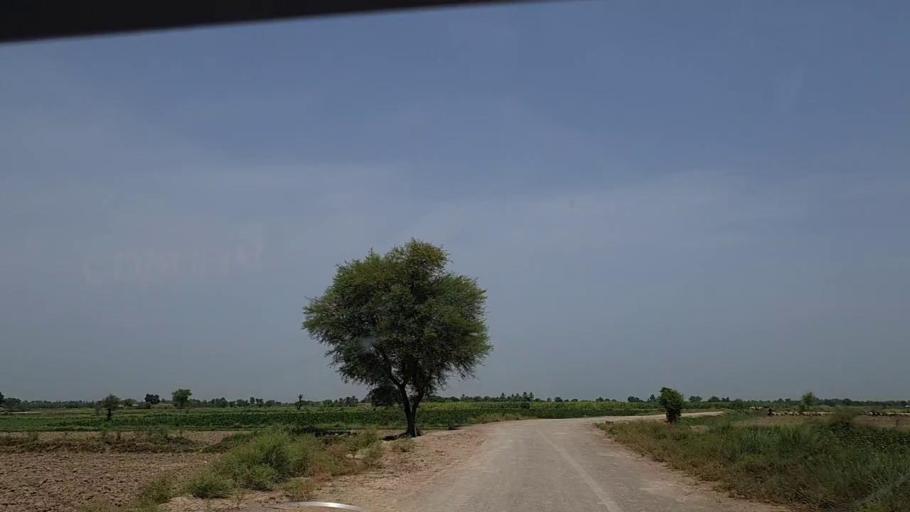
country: PK
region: Sindh
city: Tharu Shah
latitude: 26.9071
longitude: 68.0534
